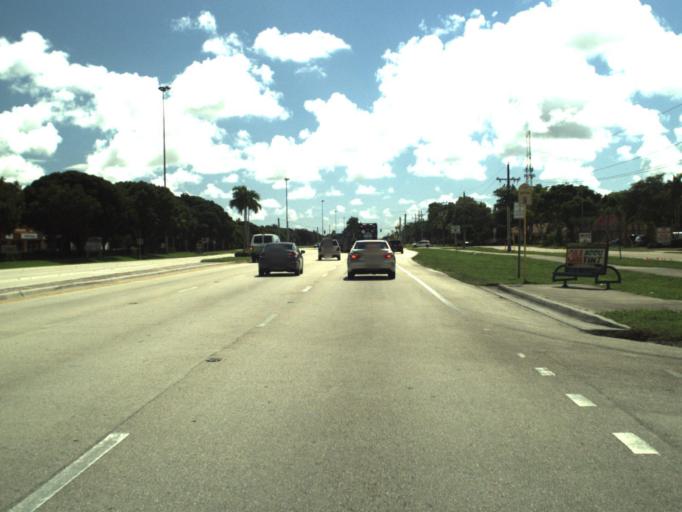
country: US
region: Florida
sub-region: Broward County
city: Cooper City
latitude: 26.0082
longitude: -80.2774
